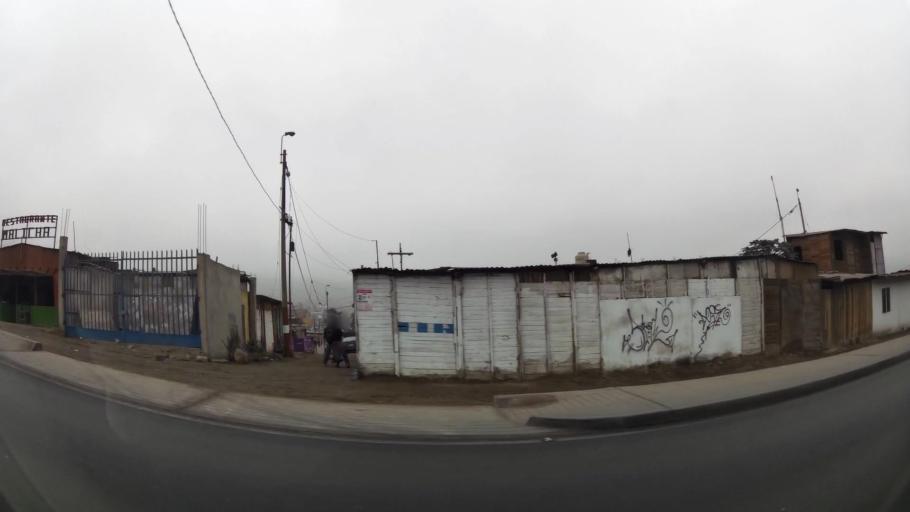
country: PE
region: Lima
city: Ventanilla
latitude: -11.8542
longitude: -77.1297
